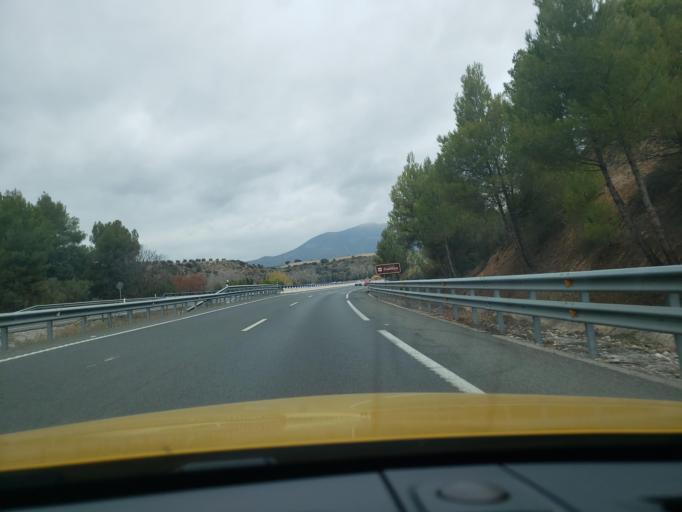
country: ES
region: Andalusia
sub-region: Provincia de Granada
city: Calicasas
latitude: 37.2991
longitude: -3.6584
